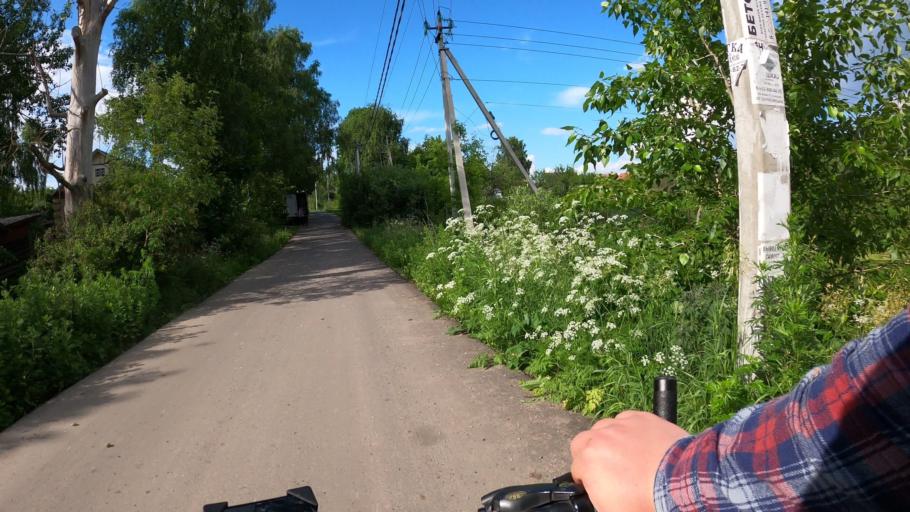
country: RU
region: Moskovskaya
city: Konobeyevo
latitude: 55.4226
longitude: 38.6502
